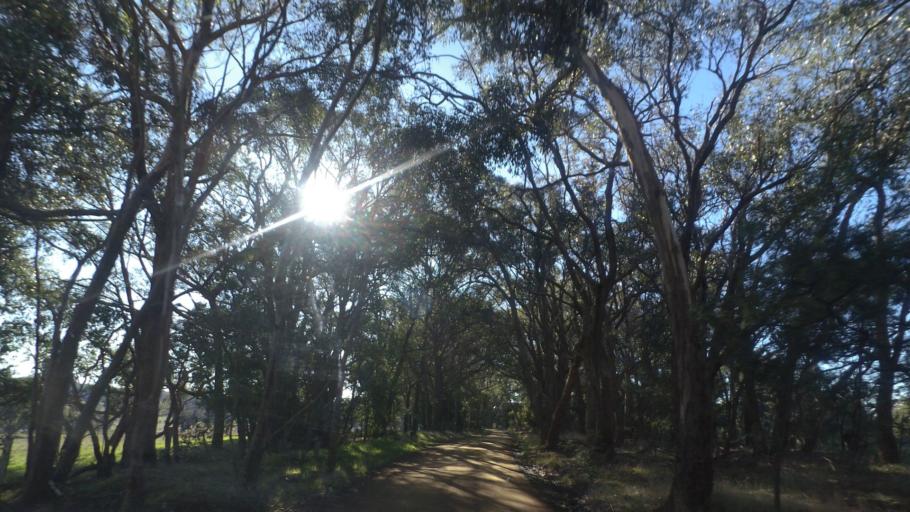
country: AU
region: Victoria
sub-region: Mount Alexander
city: Castlemaine
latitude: -37.2986
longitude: 144.3334
